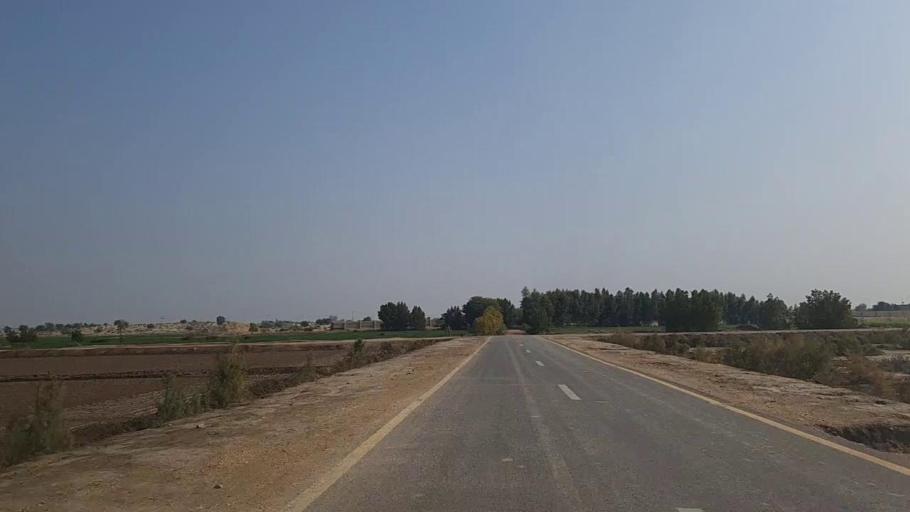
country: PK
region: Sindh
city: Jam Sahib
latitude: 26.3706
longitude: 68.5359
